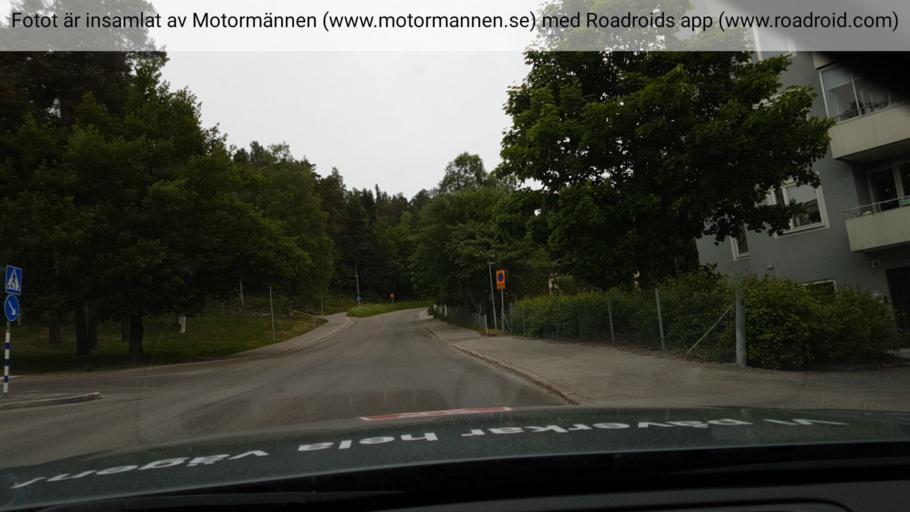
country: SE
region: Vaesternorrland
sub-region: Sundsvalls Kommun
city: Sundsvall
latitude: 62.3955
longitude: 17.3040
